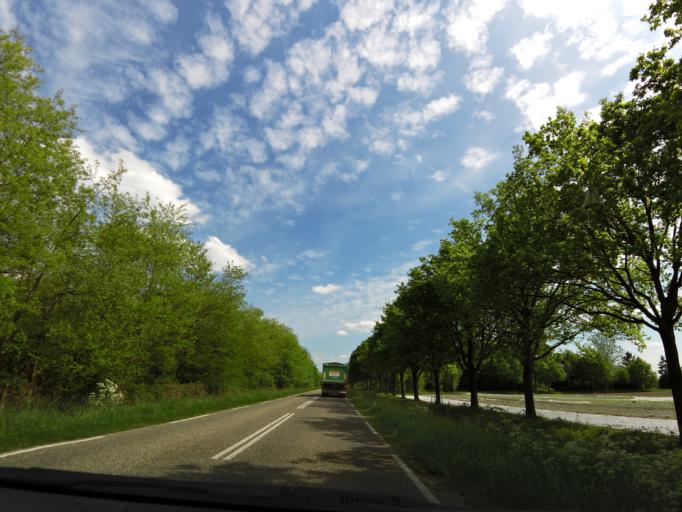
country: NL
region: Limburg
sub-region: Gemeente Leudal
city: Haelen
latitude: 51.2923
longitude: 5.9649
